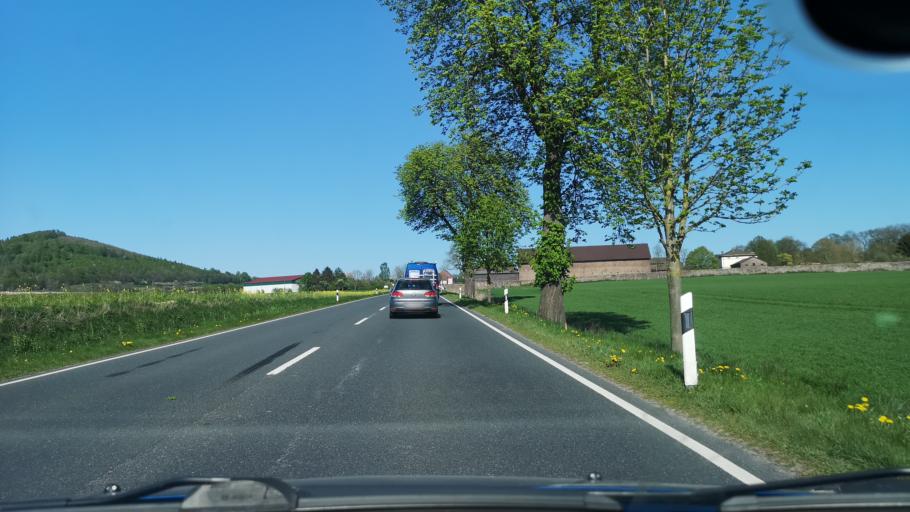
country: DE
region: Lower Saxony
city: Holenberg
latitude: 51.8958
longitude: 9.5882
